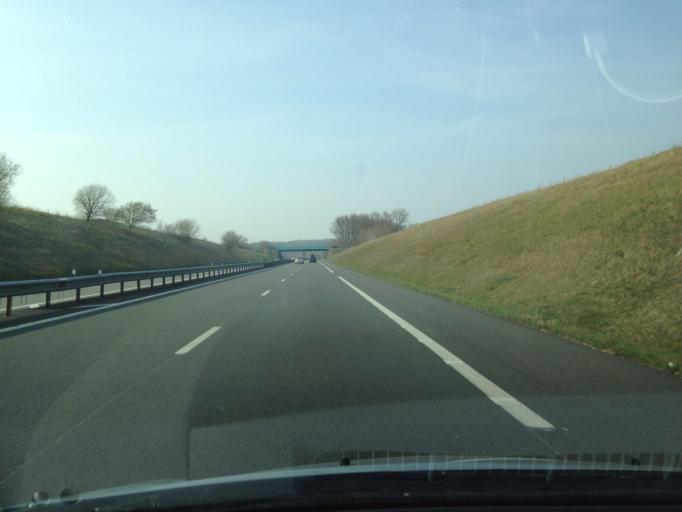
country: FR
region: Picardie
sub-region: Departement de la Somme
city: Rue
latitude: 50.2647
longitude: 1.7425
